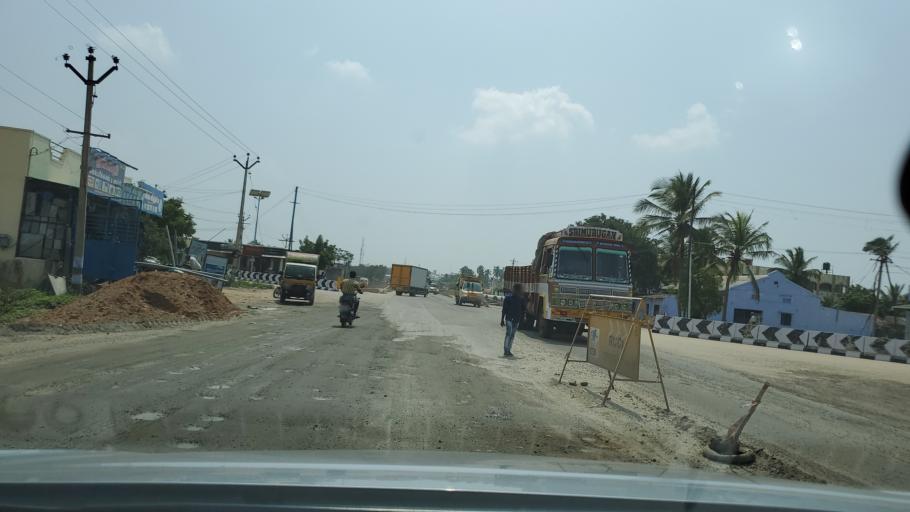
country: IN
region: Tamil Nadu
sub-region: Tiruppur
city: Dharapuram
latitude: 10.7479
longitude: 77.5188
